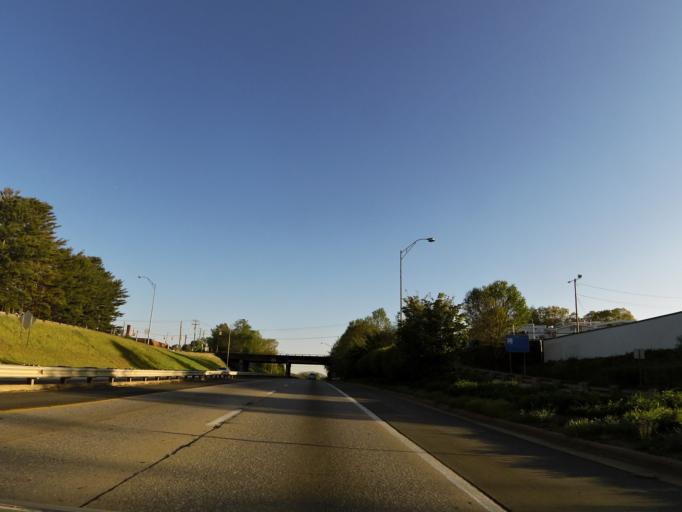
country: US
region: North Carolina
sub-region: Buncombe County
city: Asheville
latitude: 35.5794
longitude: -82.5827
